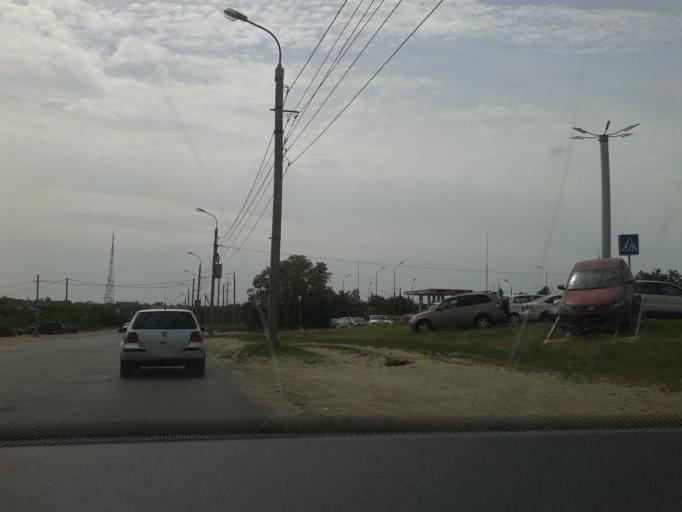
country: RU
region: Volgograd
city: Volgograd
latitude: 48.7566
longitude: 44.5235
